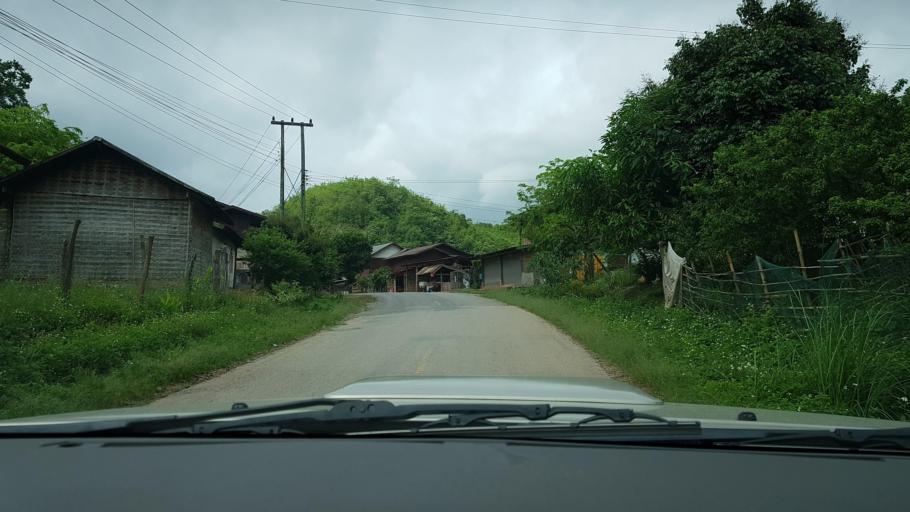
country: LA
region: Oudomxai
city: Muang Xay
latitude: 20.5731
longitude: 101.9207
